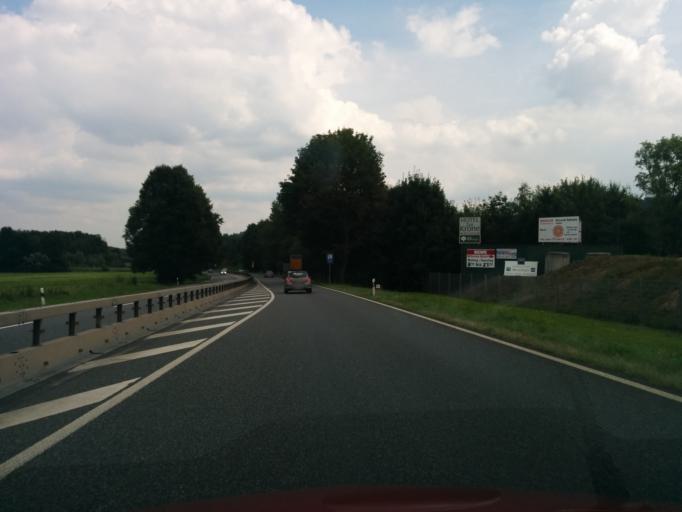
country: DE
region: Hesse
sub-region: Regierungsbezirk Giessen
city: Lohnberg
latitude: 50.5171
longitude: 8.2660
